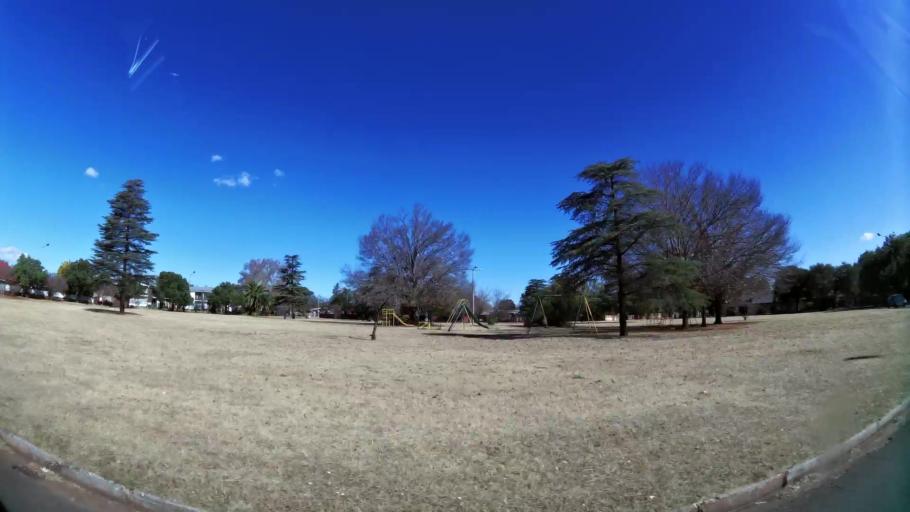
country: ZA
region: Gauteng
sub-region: West Rand District Municipality
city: Carletonville
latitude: -26.3477
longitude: 27.3876
